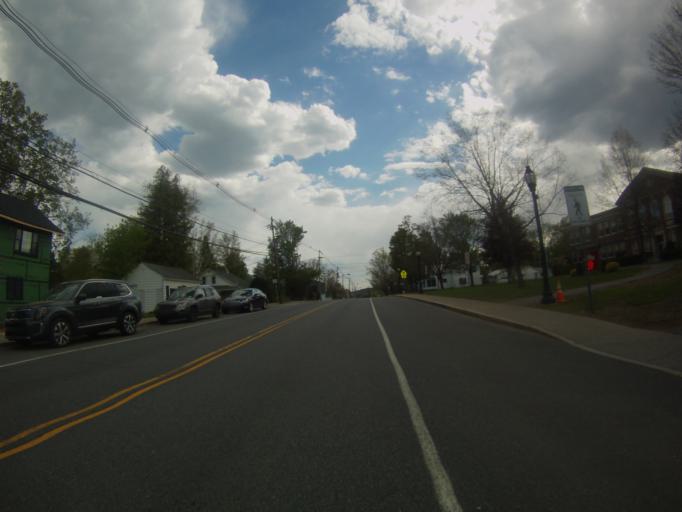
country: US
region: New York
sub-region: Essex County
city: Ticonderoga
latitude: 43.8393
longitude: -73.7609
